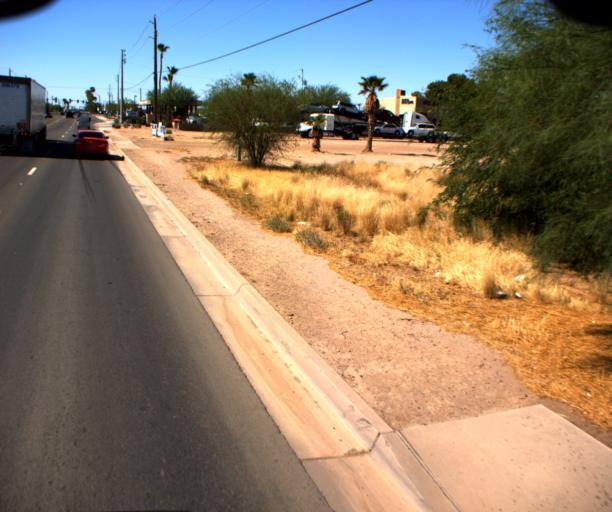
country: US
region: Arizona
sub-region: Pinal County
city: Casa Grande
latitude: 32.8968
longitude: -111.7574
